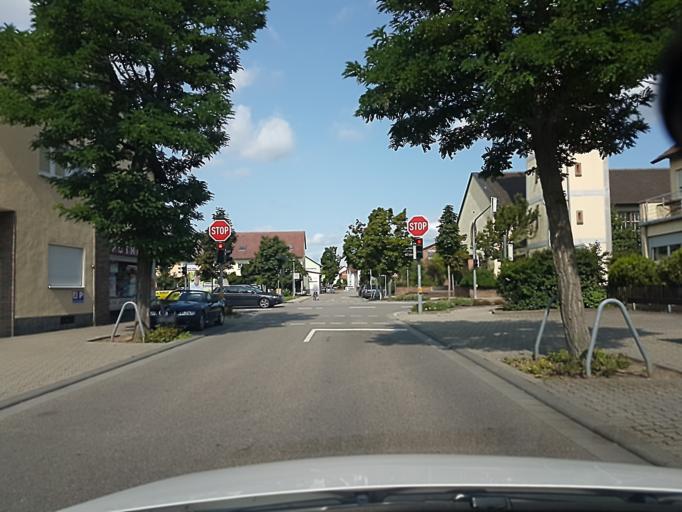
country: DE
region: Rheinland-Pfalz
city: Schifferstadt
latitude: 49.3797
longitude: 8.3852
